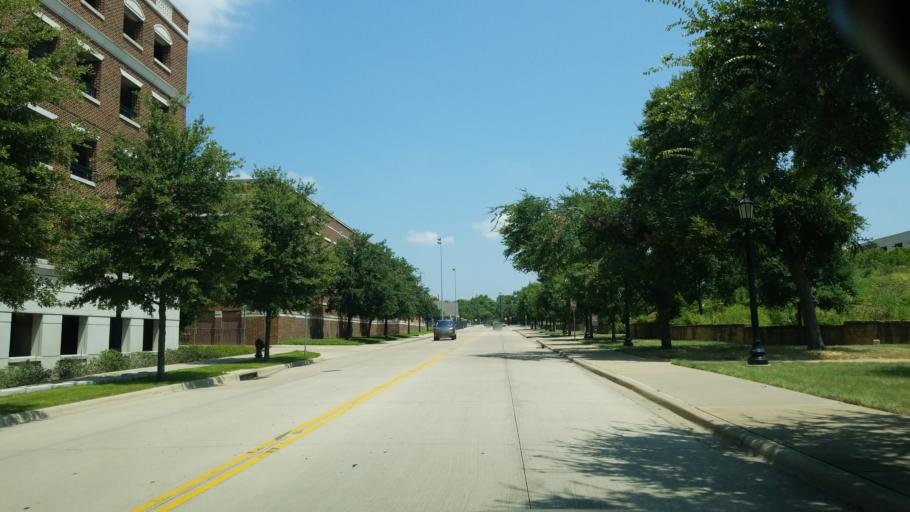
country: US
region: Texas
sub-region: Dallas County
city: Highland Park
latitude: 32.8397
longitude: -96.7794
